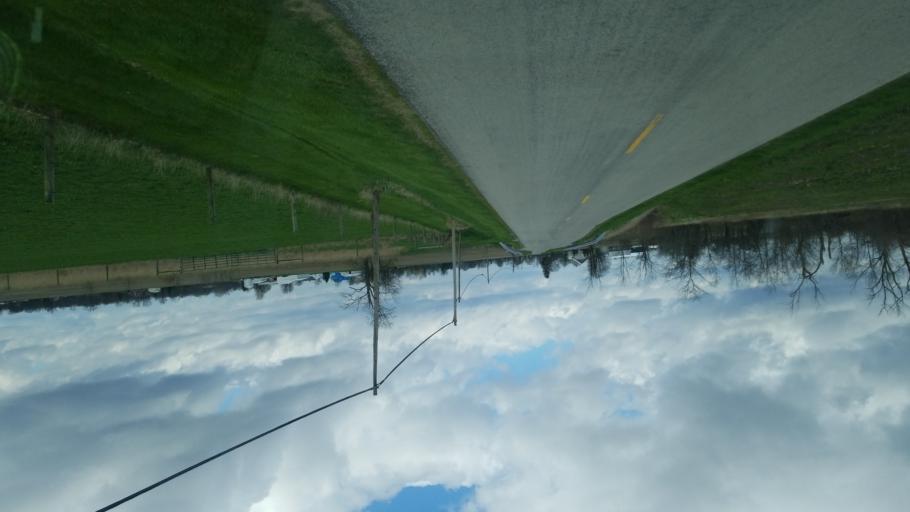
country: US
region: Ohio
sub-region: Union County
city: Richwood
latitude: 40.4120
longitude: -83.3098
